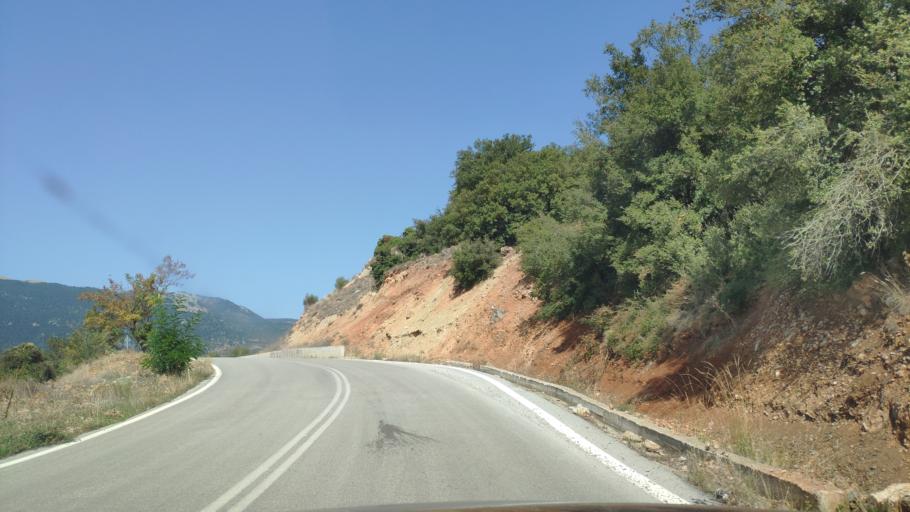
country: GR
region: West Greece
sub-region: Nomos Achaias
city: Aiyira
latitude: 37.9222
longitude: 22.3390
